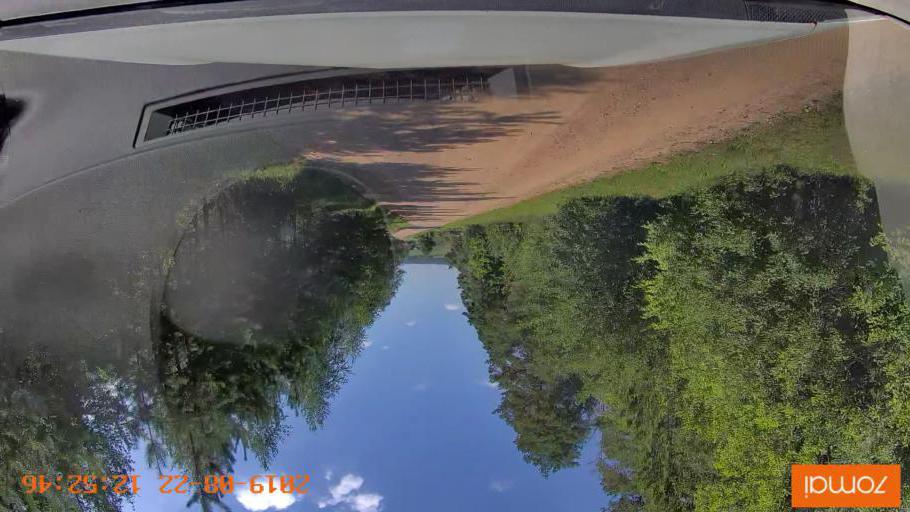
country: BY
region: Minsk
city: Prawdzinski
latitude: 53.4509
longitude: 27.6789
